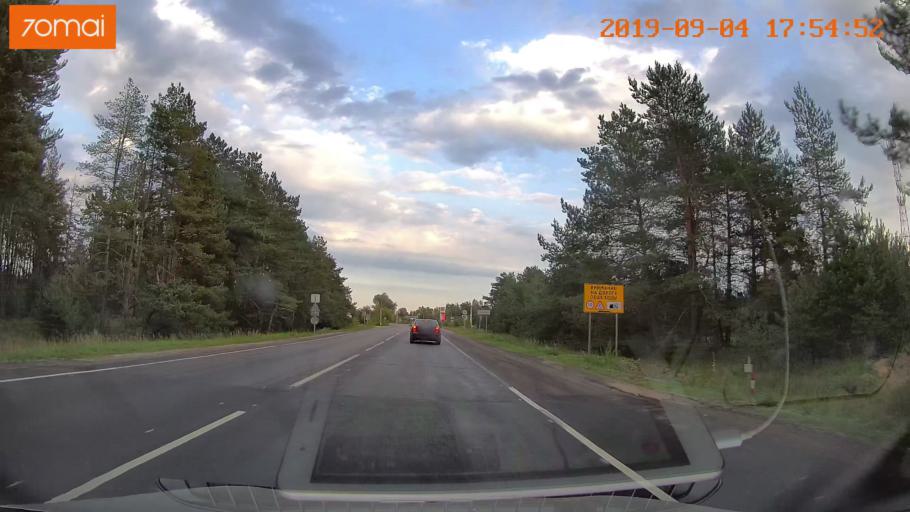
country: RU
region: Moskovskaya
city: Imeni Tsyurupy
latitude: 55.5084
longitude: 38.7567
